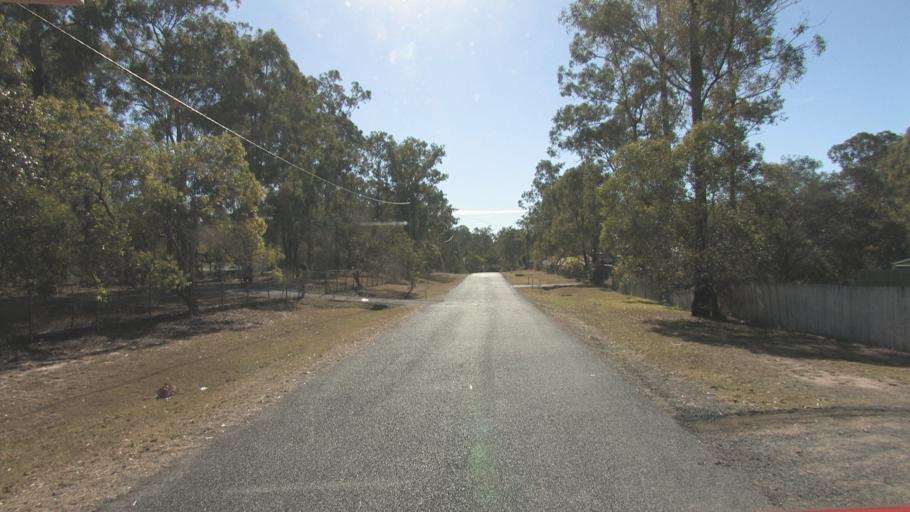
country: AU
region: Queensland
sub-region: Logan
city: North Maclean
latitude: -27.8095
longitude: 152.9666
